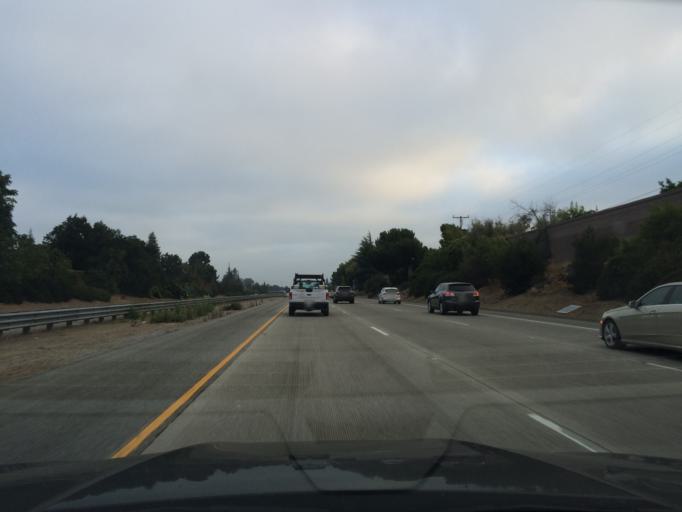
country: US
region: California
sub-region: Santa Clara County
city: Saratoga
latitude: 37.2889
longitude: -122.0217
